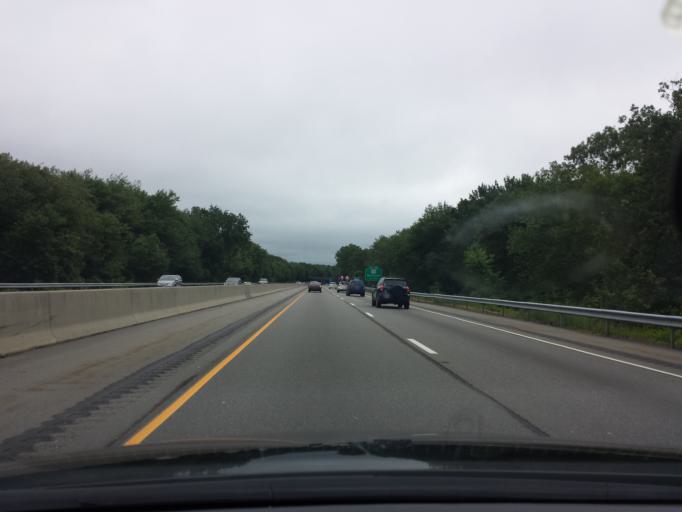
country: US
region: Connecticut
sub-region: Middlesex County
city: Westbrook Center
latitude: 41.2914
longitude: -72.4583
